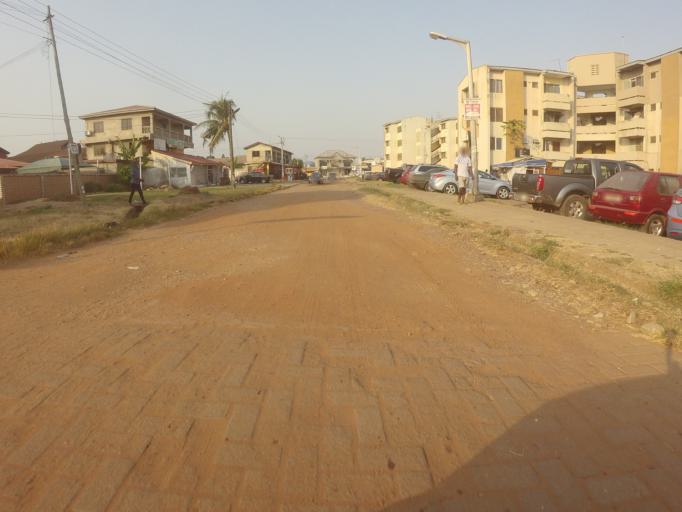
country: GH
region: Greater Accra
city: Nungua
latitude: 5.6250
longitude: -0.0637
